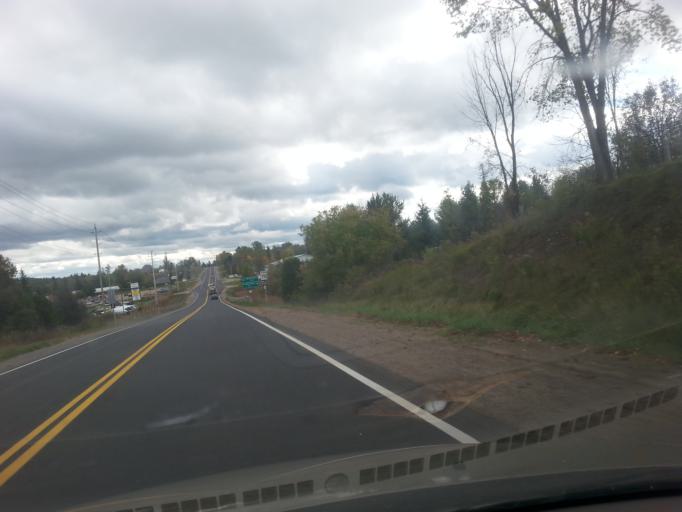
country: CA
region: Ontario
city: Pembroke
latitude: 45.5570
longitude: -77.1142
